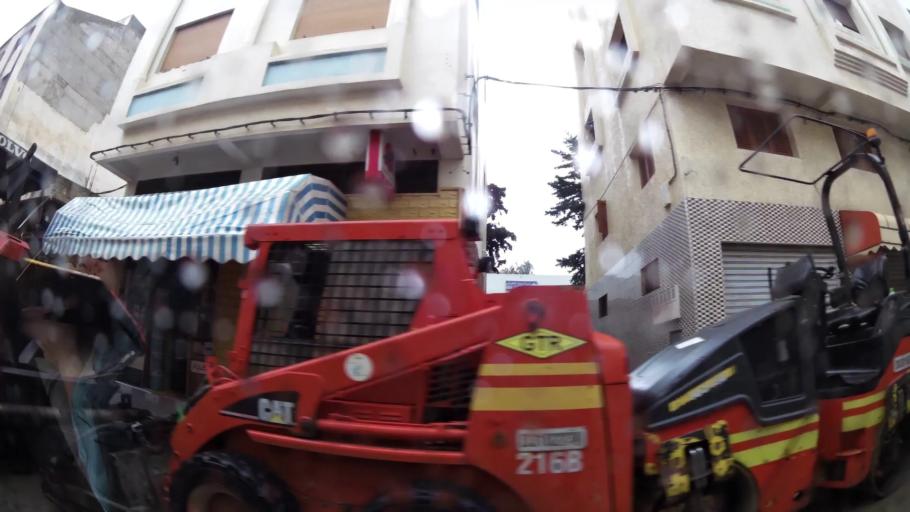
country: MA
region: Taza-Al Hoceima-Taounate
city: Al Hoceima
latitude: 35.2492
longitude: -3.9479
